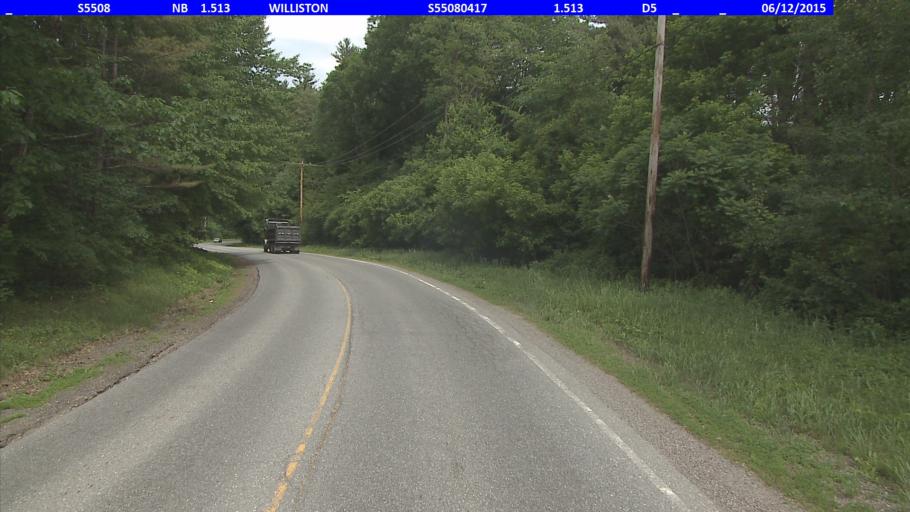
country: US
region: Vermont
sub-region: Chittenden County
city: Williston
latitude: 44.4567
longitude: -73.0547
